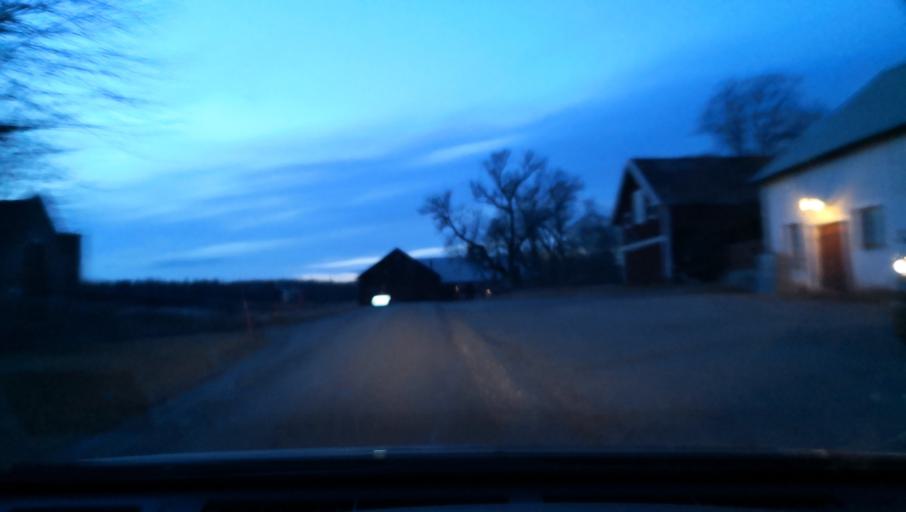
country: SE
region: Uppsala
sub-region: Enkopings Kommun
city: Dalby
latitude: 59.5748
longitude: 17.3772
